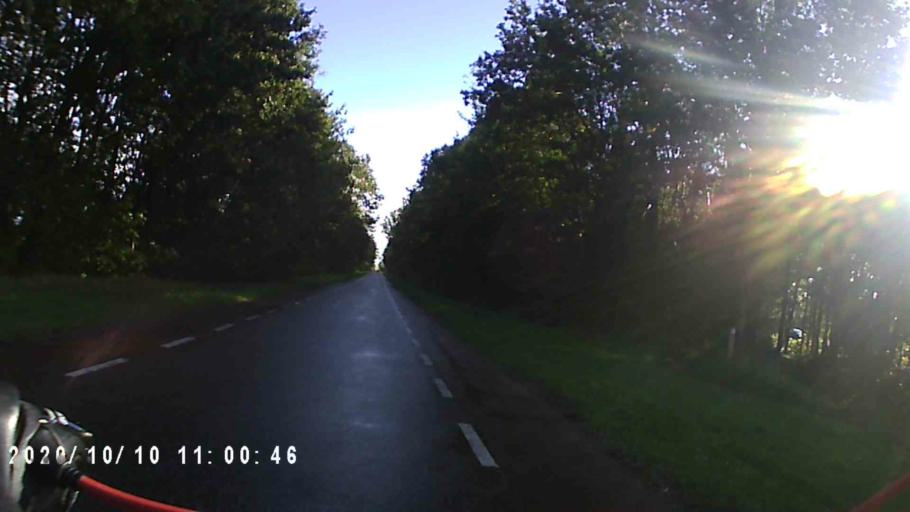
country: NL
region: Friesland
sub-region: Gemeente Achtkarspelen
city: Surhuisterveen
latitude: 53.1384
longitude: 6.2128
